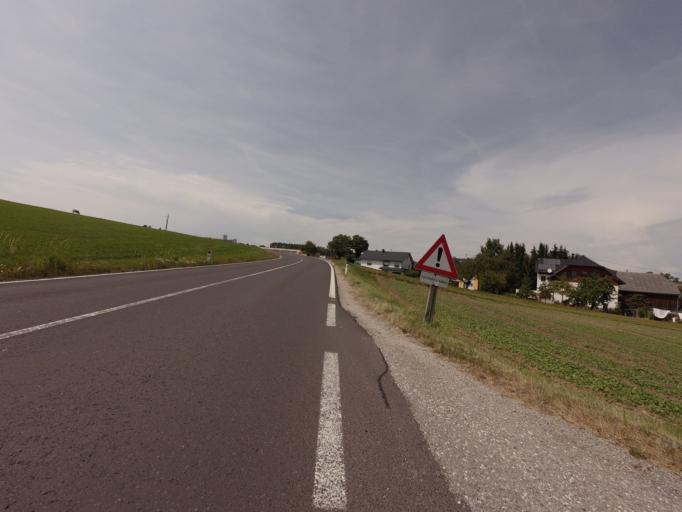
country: AT
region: Upper Austria
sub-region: Politischer Bezirk Urfahr-Umgebung
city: Bad Leonfelden
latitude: 48.5232
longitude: 14.3135
